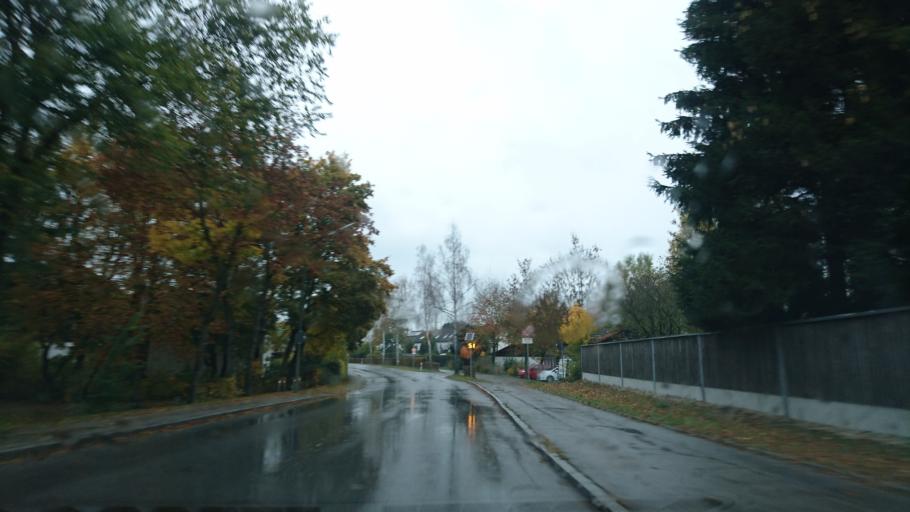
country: DE
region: Bavaria
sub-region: Upper Bavaria
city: Petershausen
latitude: 48.4061
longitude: 11.4747
